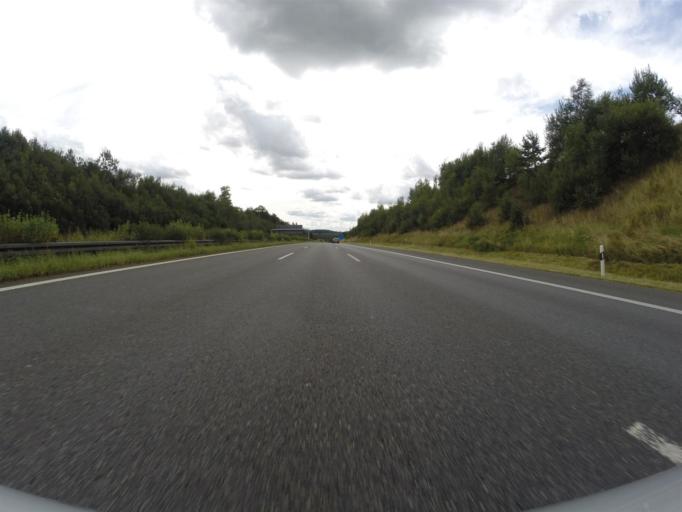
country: DE
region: Bavaria
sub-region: Upper Franconia
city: Marktschorgast
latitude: 50.0794
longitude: 11.6601
